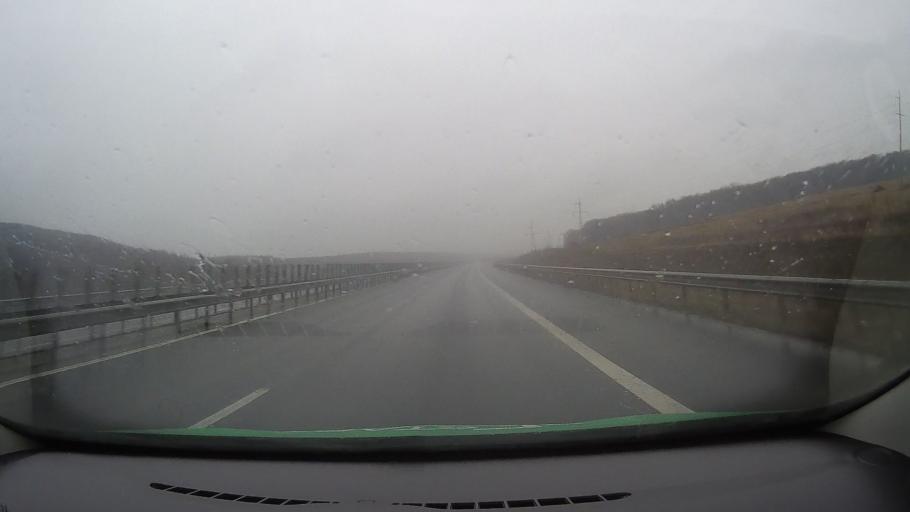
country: RO
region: Sibiu
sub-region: Comuna Cristian
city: Cristian
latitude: 45.7993
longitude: 24.0295
